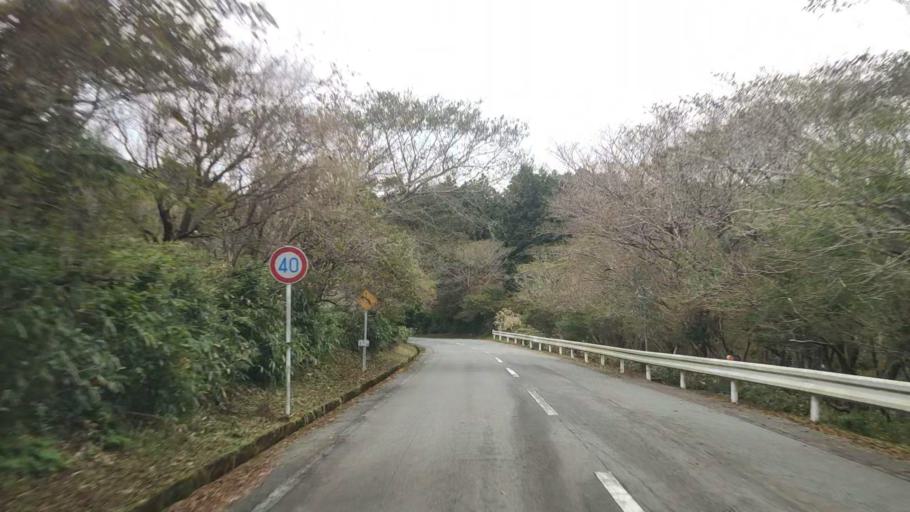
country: JP
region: Shizuoka
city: Heda
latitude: 34.9315
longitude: 138.8405
